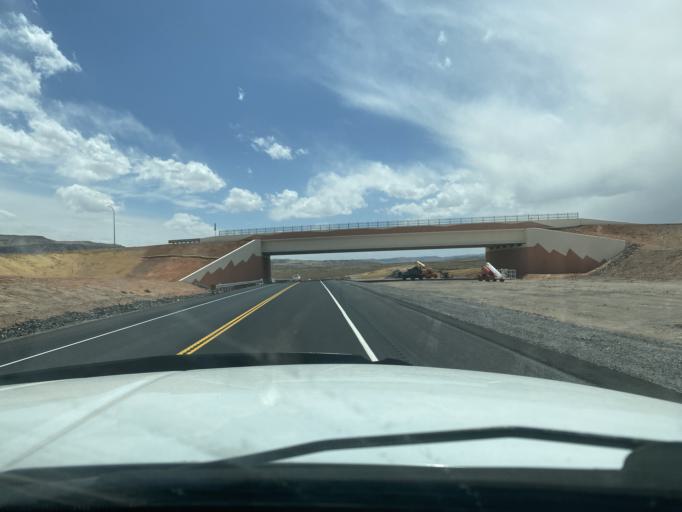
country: US
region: Utah
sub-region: Washington County
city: Hurricane
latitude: 37.1277
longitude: -113.3458
